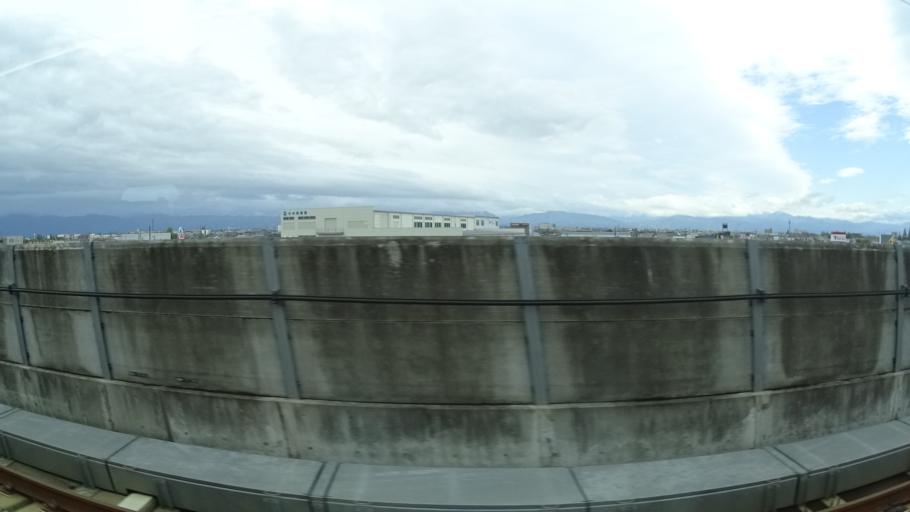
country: JP
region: Toyama
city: Toyama-shi
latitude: 36.7179
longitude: 137.2501
